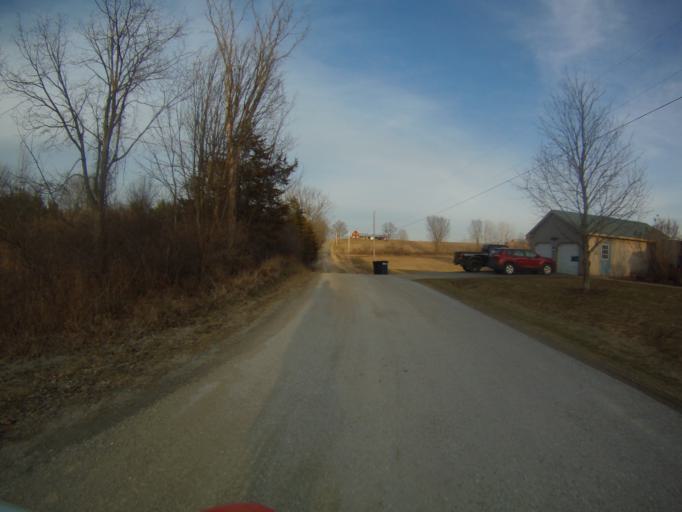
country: US
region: New York
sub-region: Essex County
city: Port Henry
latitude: 44.1178
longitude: -73.3743
